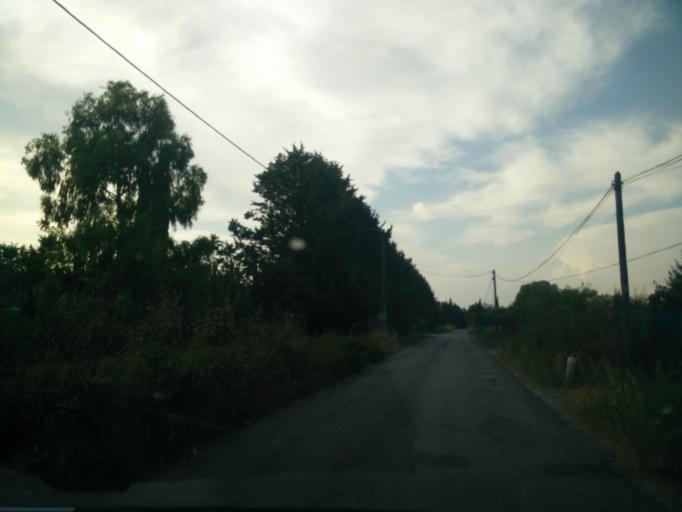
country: FR
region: Languedoc-Roussillon
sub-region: Departement de l'Herault
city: Marsillargues
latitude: 43.6758
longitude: 4.1737
